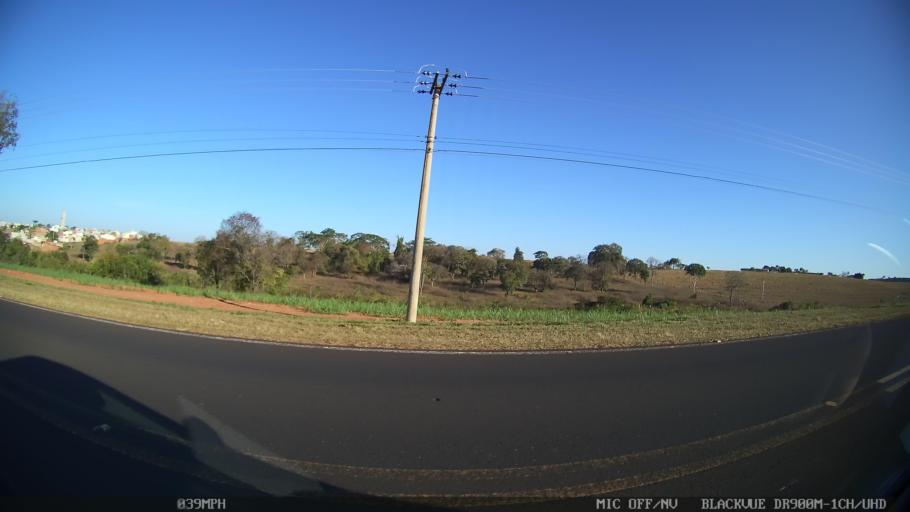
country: BR
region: Sao Paulo
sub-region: Guapiacu
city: Guapiacu
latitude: -20.7879
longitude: -49.2431
